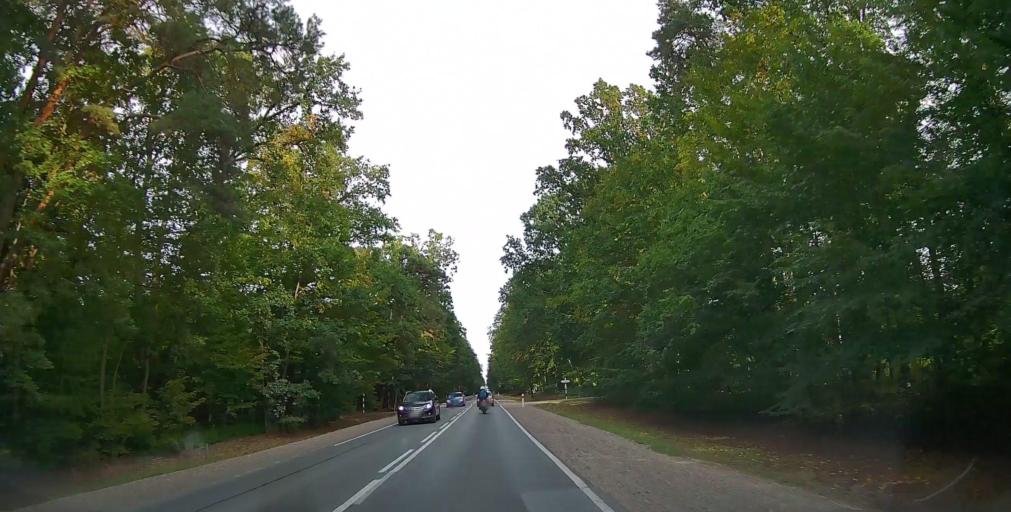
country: PL
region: Masovian Voivodeship
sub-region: Powiat piaseczynski
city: Zabieniec
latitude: 52.0471
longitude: 21.0729
